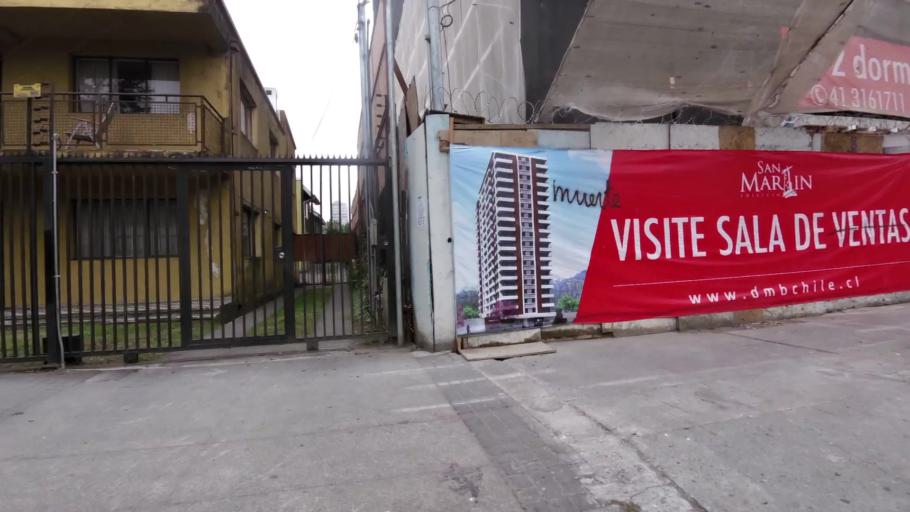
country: CL
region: Biobio
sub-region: Provincia de Concepcion
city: Concepcion
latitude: -36.8253
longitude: -73.0416
